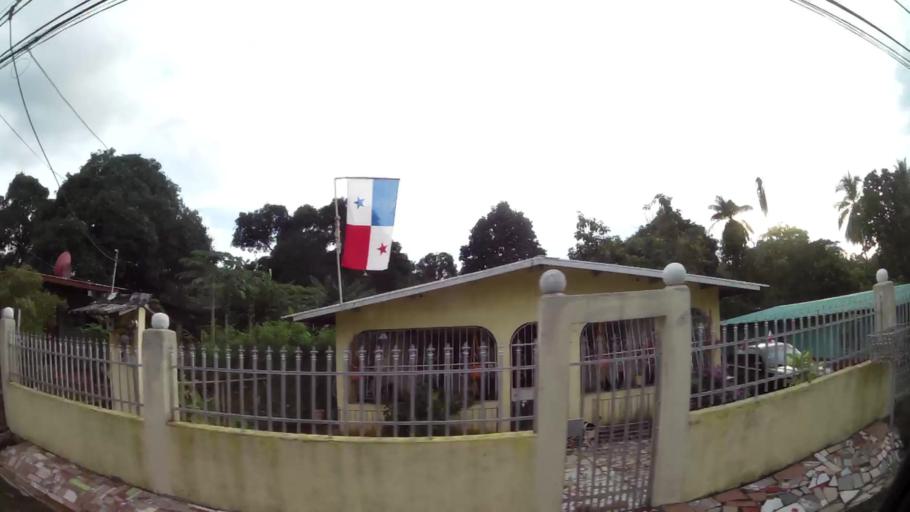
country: PA
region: Panama
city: Tocumen
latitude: 9.0938
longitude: -79.3832
